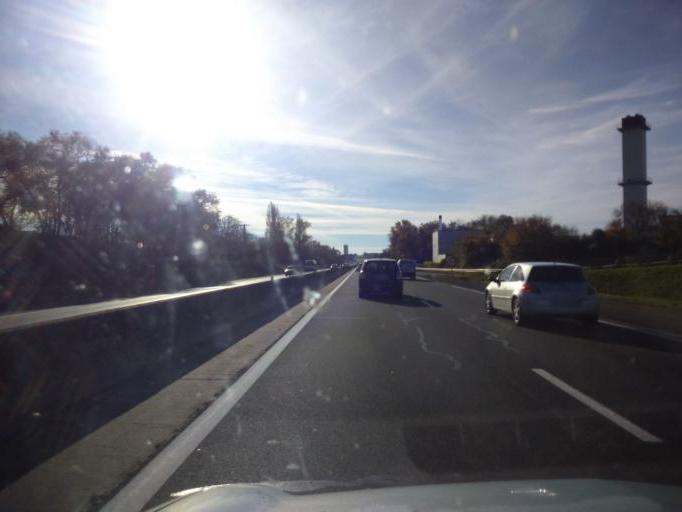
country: FR
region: Poitou-Charentes
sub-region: Departement de la Charente-Maritime
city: Perigny
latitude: 46.1524
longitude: -1.1134
